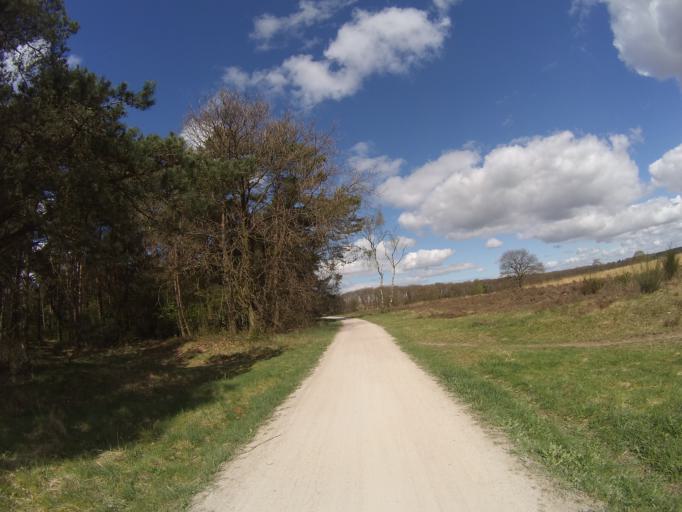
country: NL
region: North Holland
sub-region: Gemeente Bussum
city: Bussum
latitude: 52.2598
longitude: 5.1740
